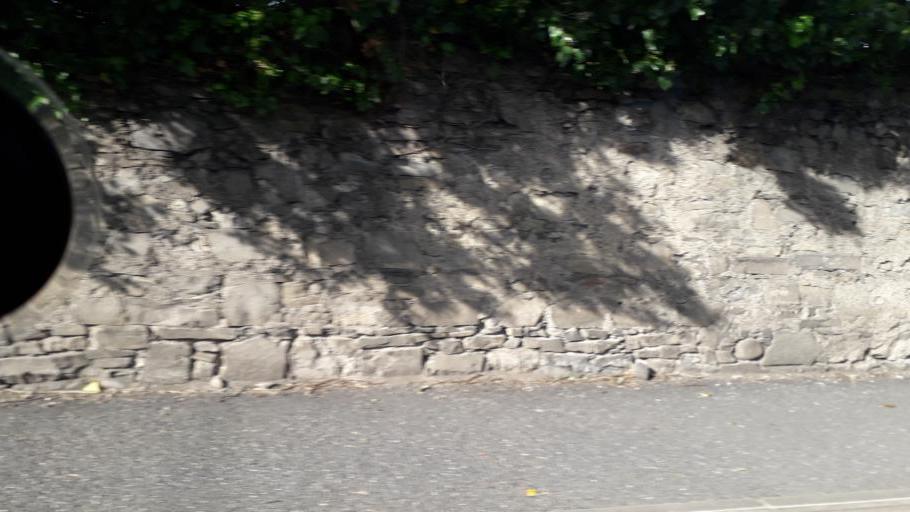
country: IE
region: Leinster
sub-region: Kildare
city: Leixlip
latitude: 53.3593
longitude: -6.4738
